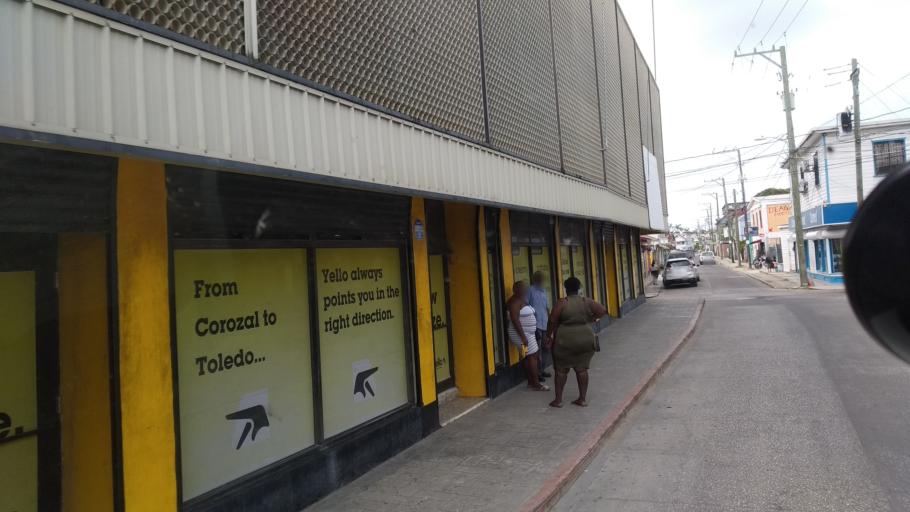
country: BZ
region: Belize
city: Belize City
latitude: 17.4977
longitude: -88.1864
